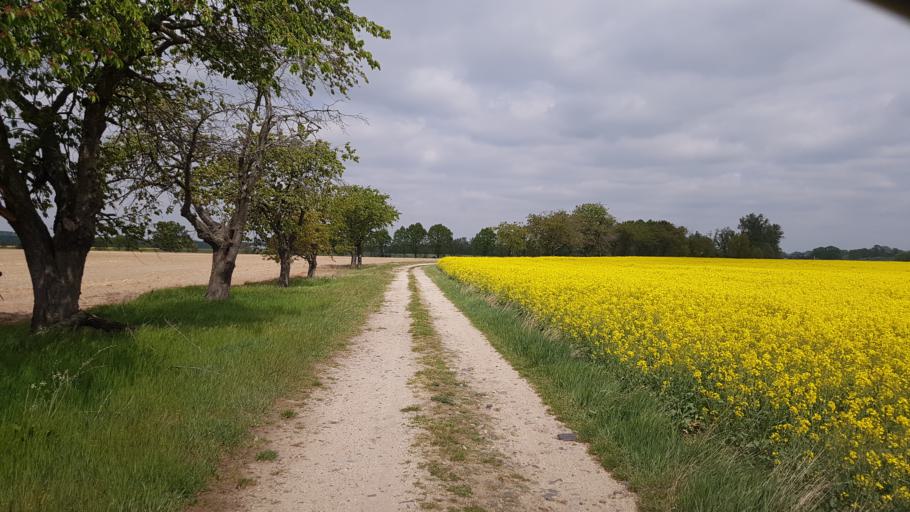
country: DE
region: Brandenburg
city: Sonnewalde
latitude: 51.6768
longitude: 13.6306
